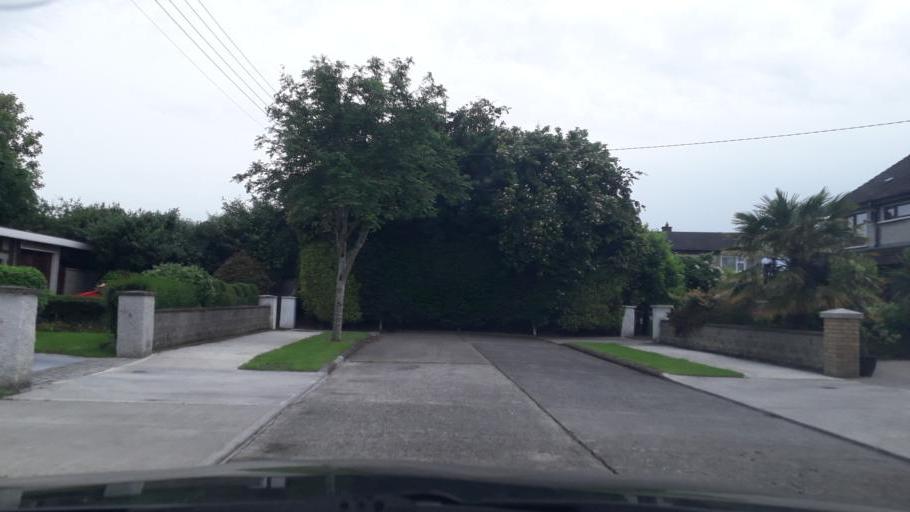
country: IE
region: Leinster
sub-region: Fingal County
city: Blanchardstown
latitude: 53.3863
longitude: -6.3831
